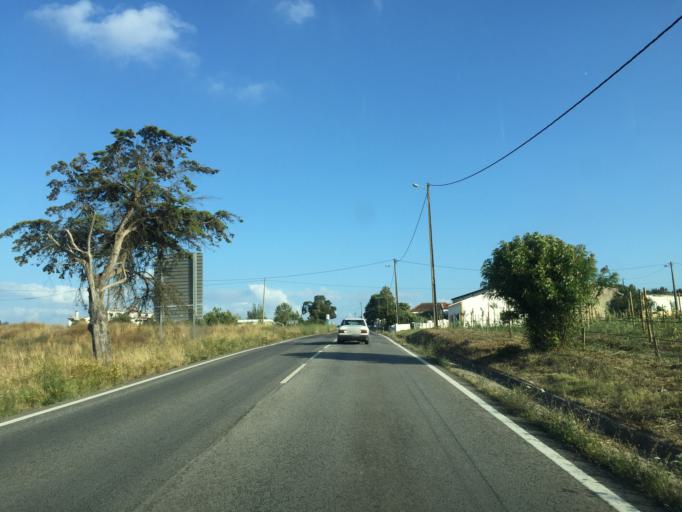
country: PT
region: Lisbon
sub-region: Alenquer
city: Alenquer
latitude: 39.1346
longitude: -8.9975
